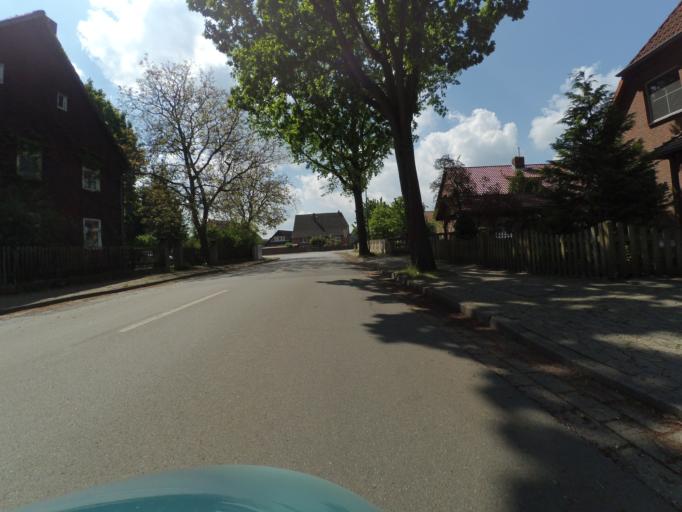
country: DE
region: Lower Saxony
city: Vechelde
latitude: 52.3067
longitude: 10.3154
